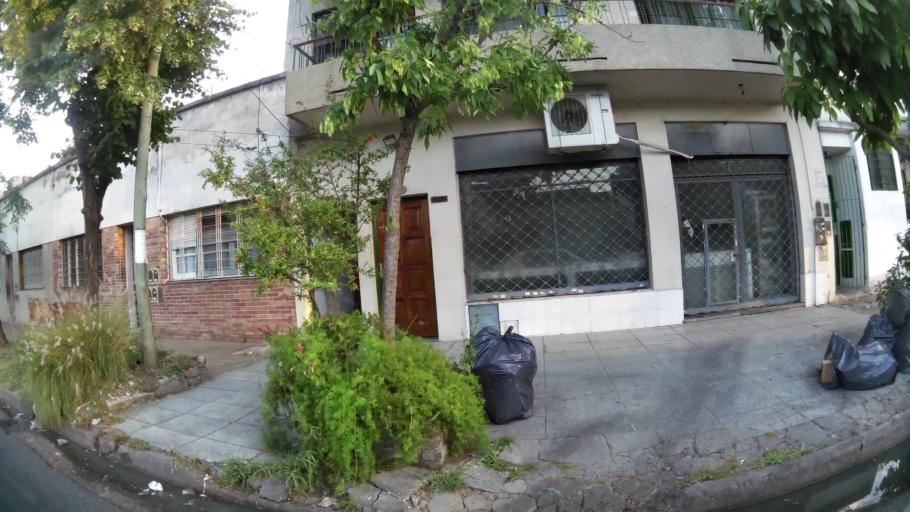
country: AR
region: Buenos Aires
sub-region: Partido de Vicente Lopez
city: Olivos
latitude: -34.5329
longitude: -58.5096
